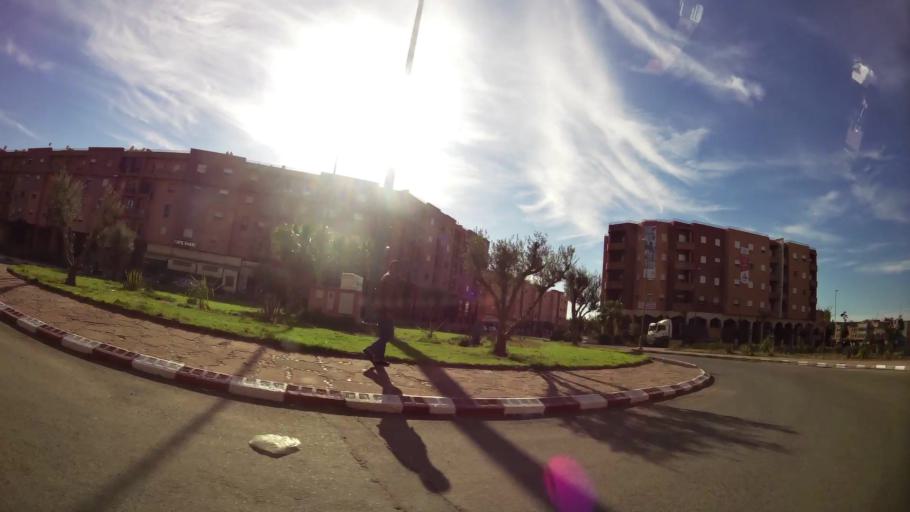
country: MA
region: Marrakech-Tensift-Al Haouz
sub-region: Marrakech
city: Marrakesh
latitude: 31.6865
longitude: -8.0688
